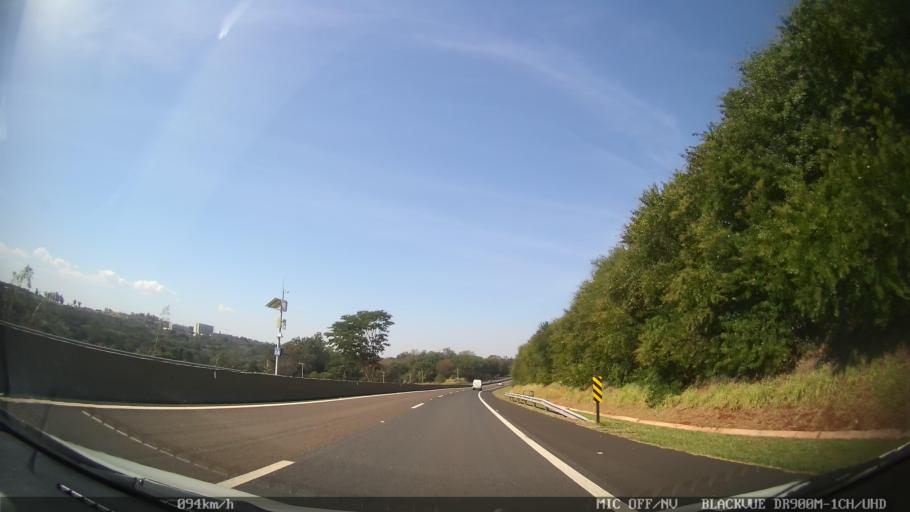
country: BR
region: Sao Paulo
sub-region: Ribeirao Preto
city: Ribeirao Preto
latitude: -21.1677
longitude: -47.8699
